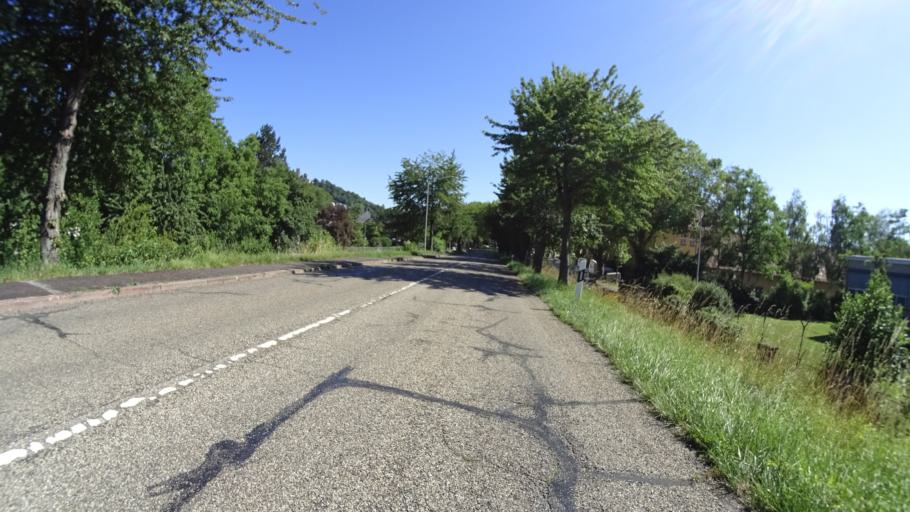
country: DE
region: Baden-Wuerttemberg
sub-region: Karlsruhe Region
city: Weingarten
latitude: 49.0065
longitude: 8.4780
